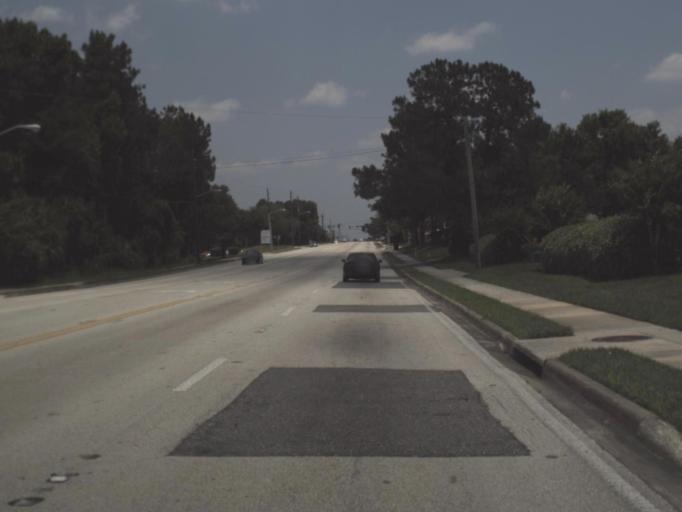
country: US
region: Florida
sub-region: Duval County
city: Jacksonville
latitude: 30.3845
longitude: -81.6902
